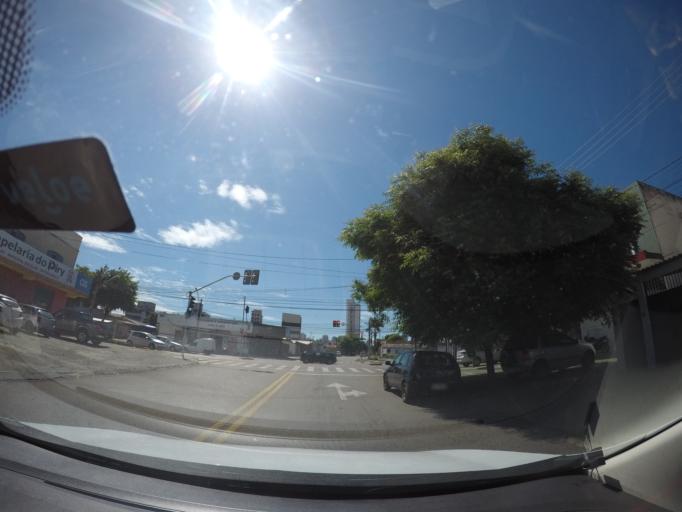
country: BR
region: Goias
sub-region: Goiania
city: Goiania
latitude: -16.6982
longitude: -49.2904
